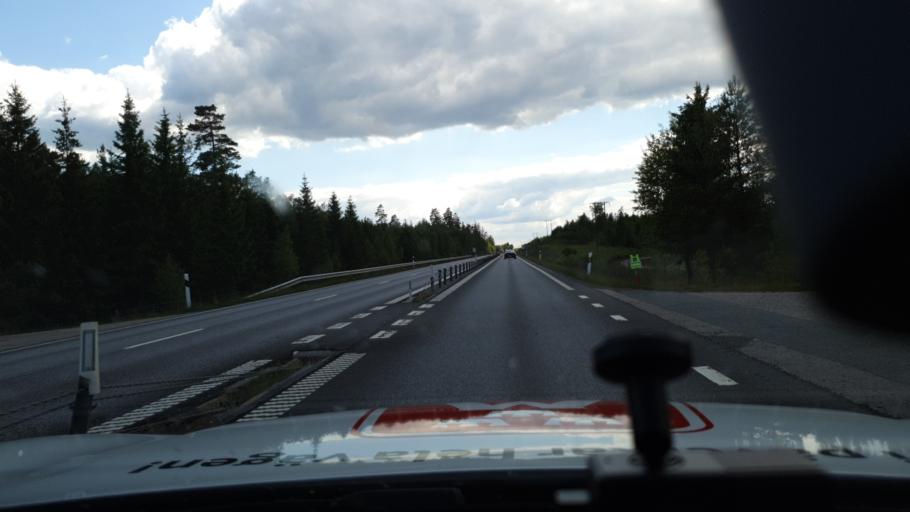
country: SE
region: Skane
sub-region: Osby Kommun
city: Osby
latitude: 56.4478
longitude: 14.0786
